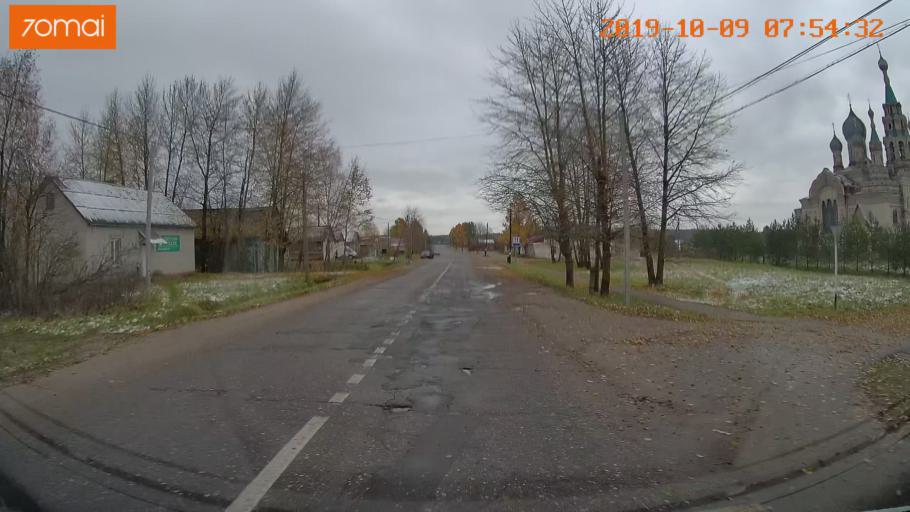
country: RU
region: Jaroslavl
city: Kukoboy
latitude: 58.6989
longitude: 39.9089
